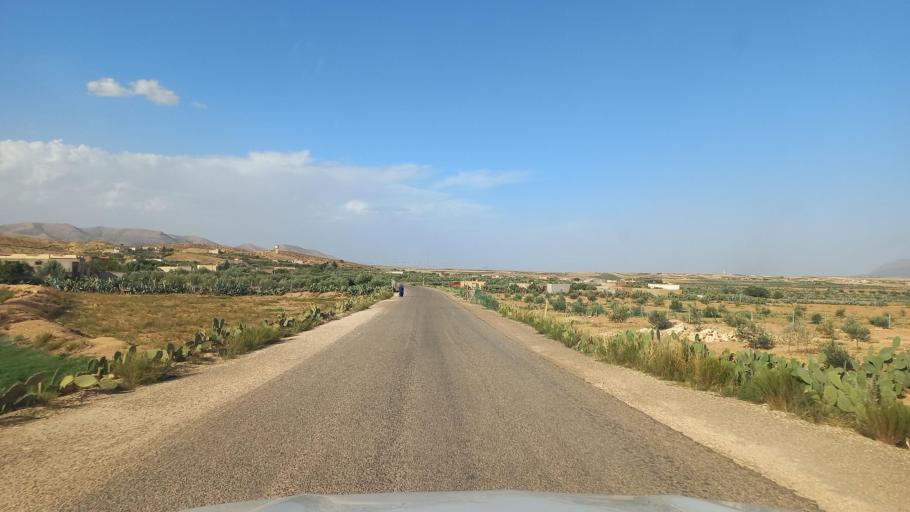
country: TN
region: Al Qasrayn
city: Sbiba
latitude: 35.3749
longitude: 9.0155
